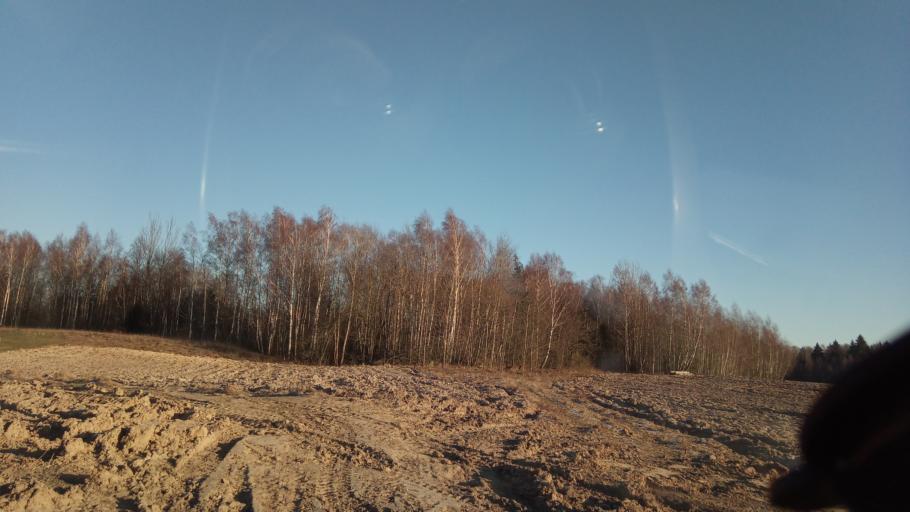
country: LT
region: Alytaus apskritis
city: Druskininkai
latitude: 54.0927
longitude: 23.9982
